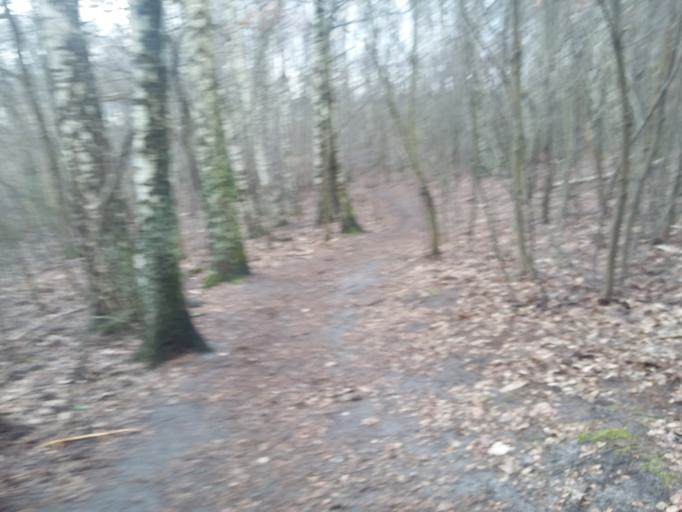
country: PL
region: Lodz Voivodeship
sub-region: Powiat pabianicki
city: Ksawerow
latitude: 51.7293
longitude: 19.4182
